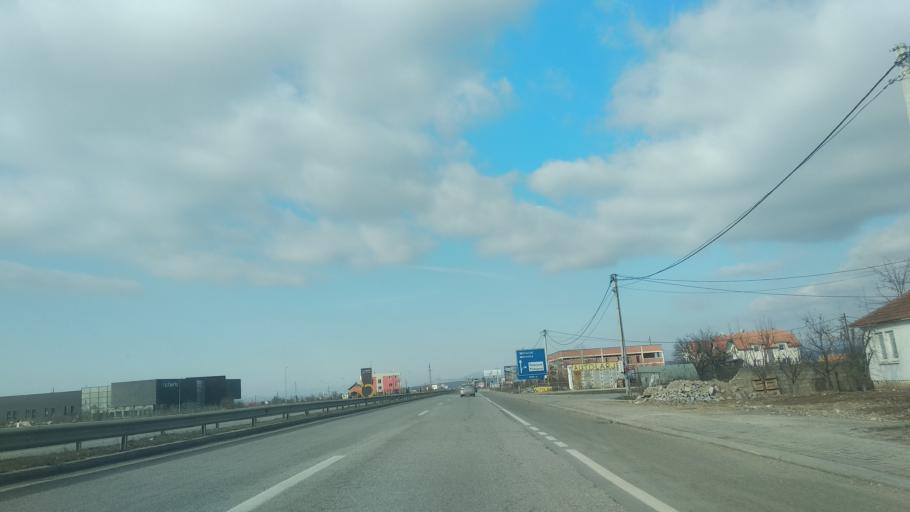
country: XK
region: Pristina
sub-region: Komuna e Obiliqit
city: Obiliq
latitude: 42.7095
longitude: 21.1029
